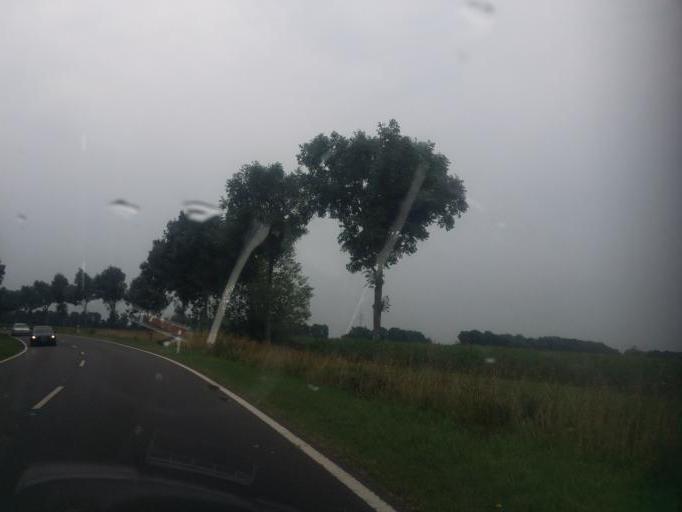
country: DE
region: Schleswig-Holstein
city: Husum
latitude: 54.4555
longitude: 9.0430
